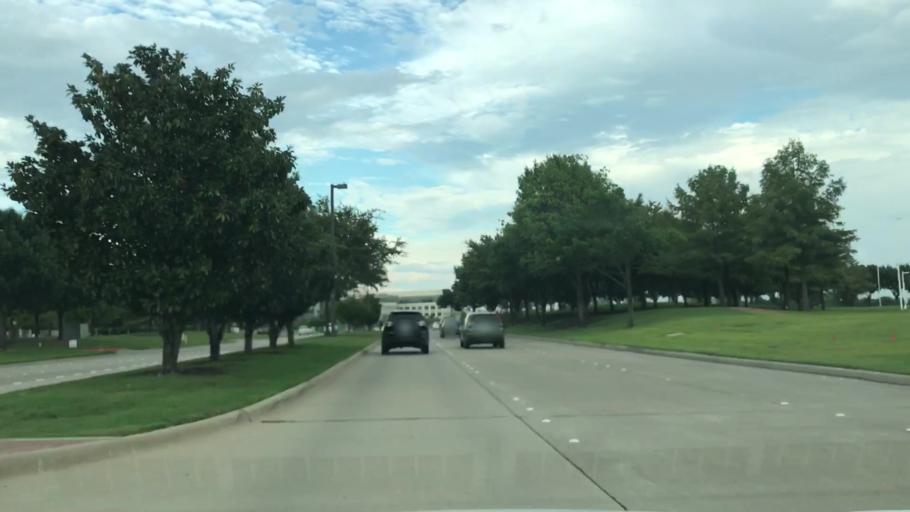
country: US
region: Texas
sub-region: Collin County
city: Frisco
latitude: 33.0840
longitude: -96.8155
